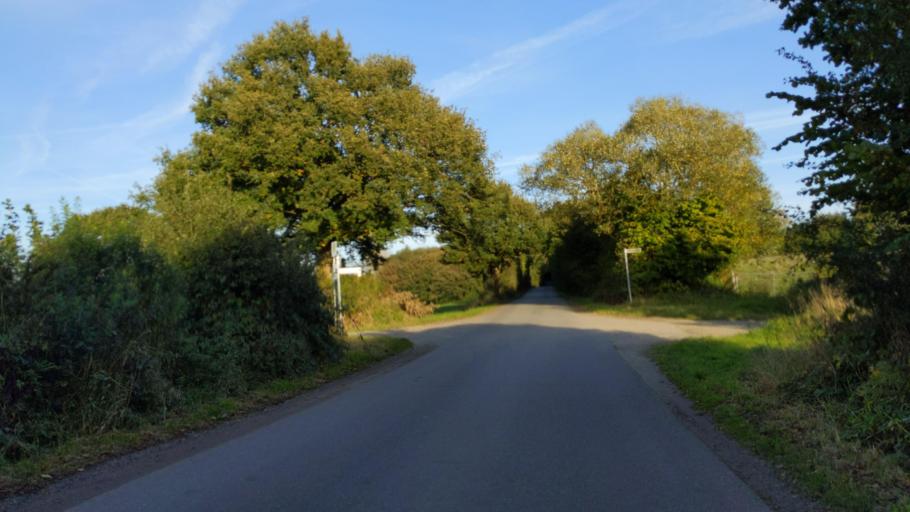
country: DE
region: Schleswig-Holstein
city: Susel
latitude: 54.0843
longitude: 10.6744
